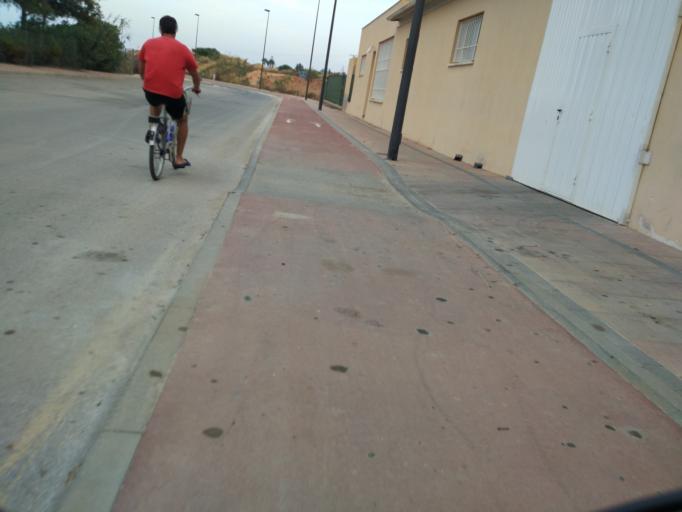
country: ES
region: Murcia
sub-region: Murcia
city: Los Alcazares
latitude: 37.7211
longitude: -0.8690
